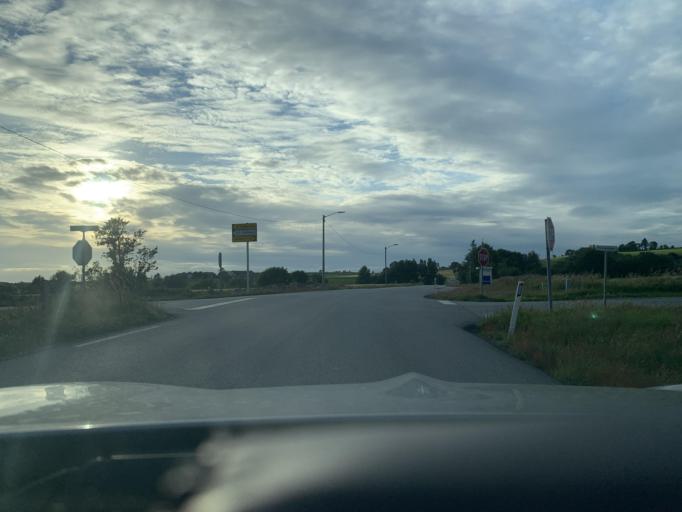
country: NO
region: Rogaland
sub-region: Time
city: Bryne
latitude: 58.7037
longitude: 5.6973
